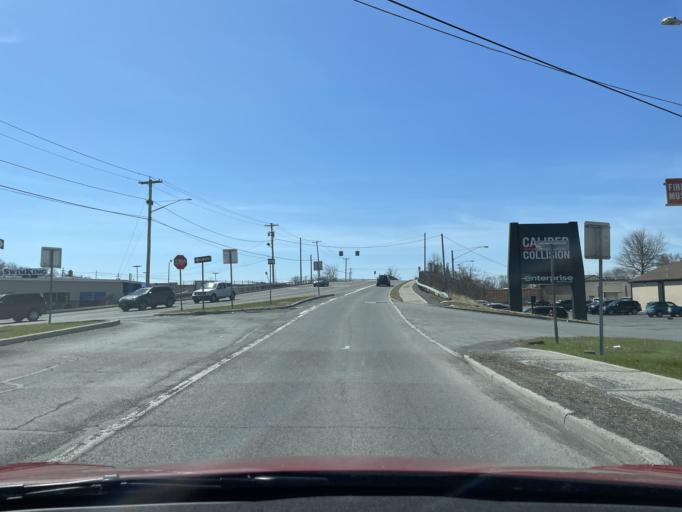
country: US
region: New York
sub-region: Ulster County
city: Lincoln Park
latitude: 41.9607
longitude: -73.9908
